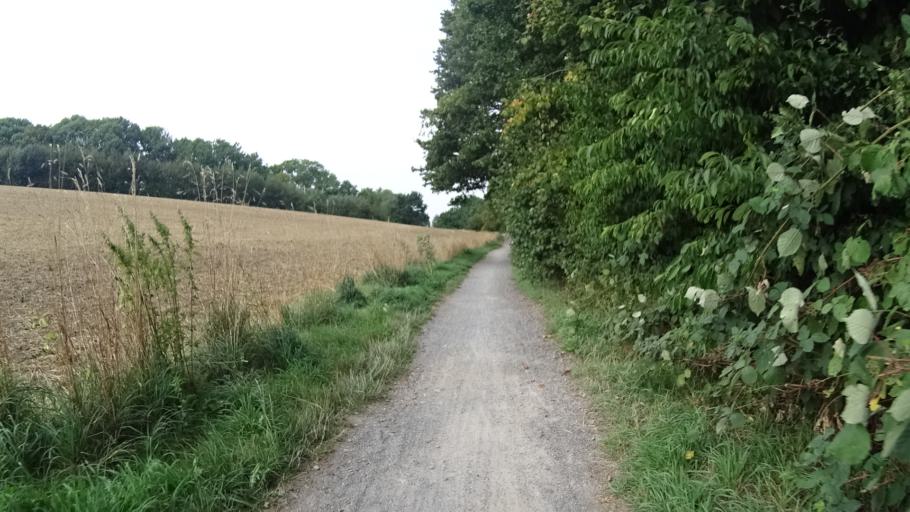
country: DE
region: North Rhine-Westphalia
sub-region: Regierungsbezirk Arnsberg
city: Dortmund
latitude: 51.4884
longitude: 7.4323
